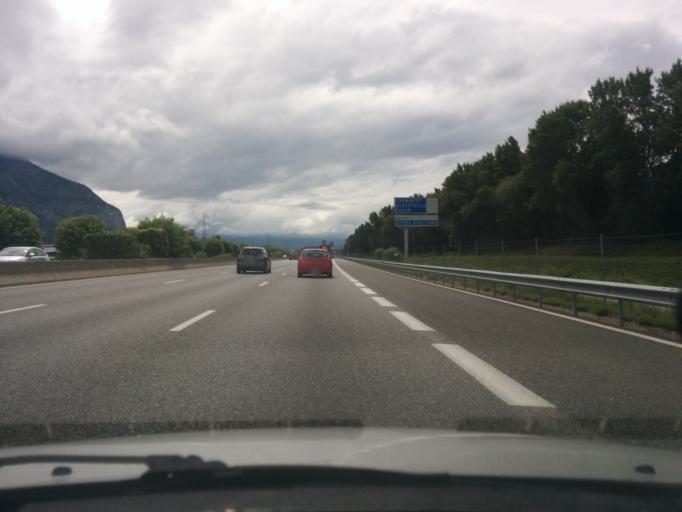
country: FR
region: Rhone-Alpes
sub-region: Departement de l'Isere
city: Fontanil-Cornillon
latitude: 45.2475
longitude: 5.6547
